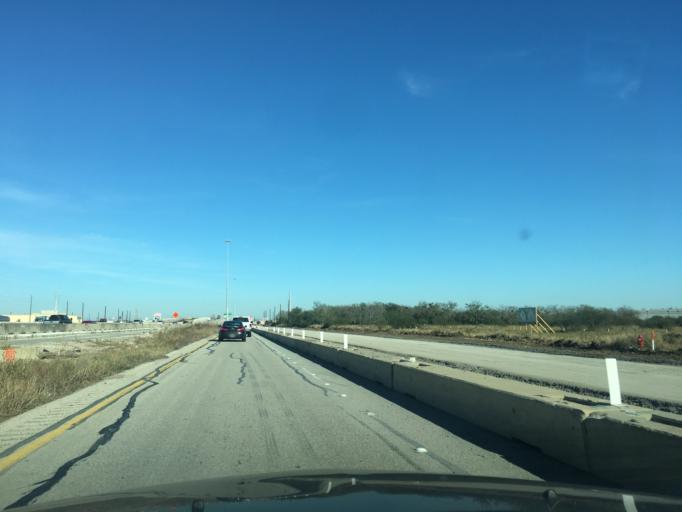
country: US
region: Texas
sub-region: Fort Bend County
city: Richmond
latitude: 29.5391
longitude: -95.7628
